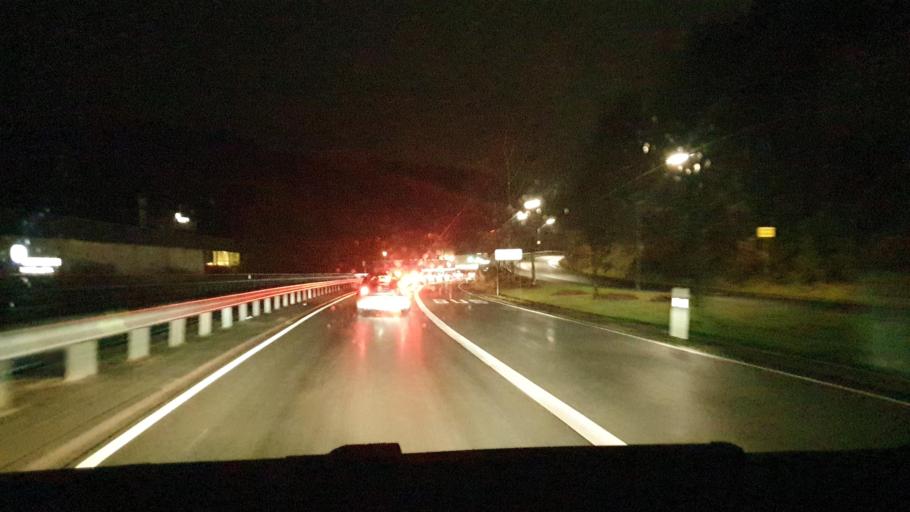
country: DE
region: North Rhine-Westphalia
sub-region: Regierungsbezirk Arnsberg
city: Siegen
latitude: 50.8895
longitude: 7.9895
